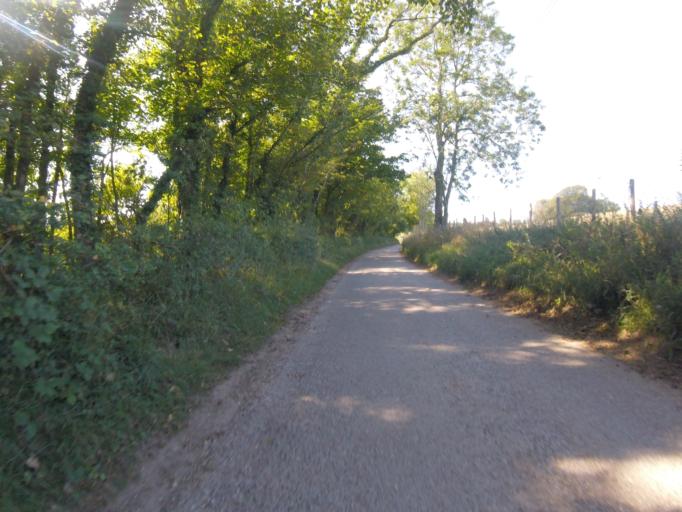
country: GB
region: England
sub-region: Brighton and Hove
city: Brighton
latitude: 50.8734
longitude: -0.1117
